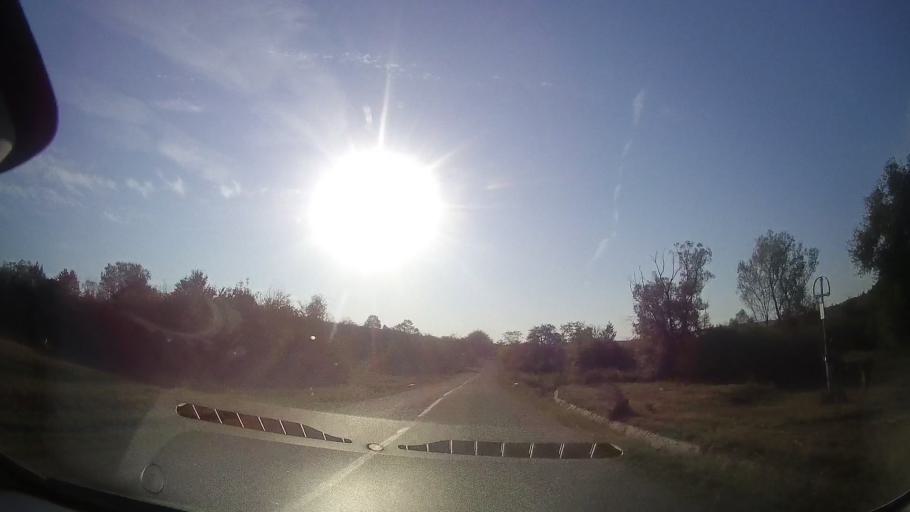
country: RO
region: Timis
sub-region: Comuna Bogda
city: Bogda
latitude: 45.9690
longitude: 21.6057
